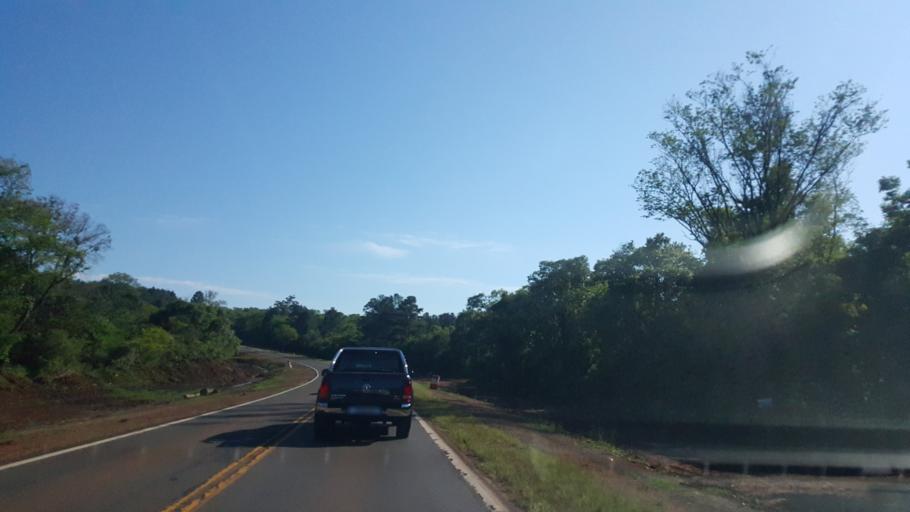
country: AR
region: Misiones
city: Santa Ana
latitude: -27.3645
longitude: -55.5582
